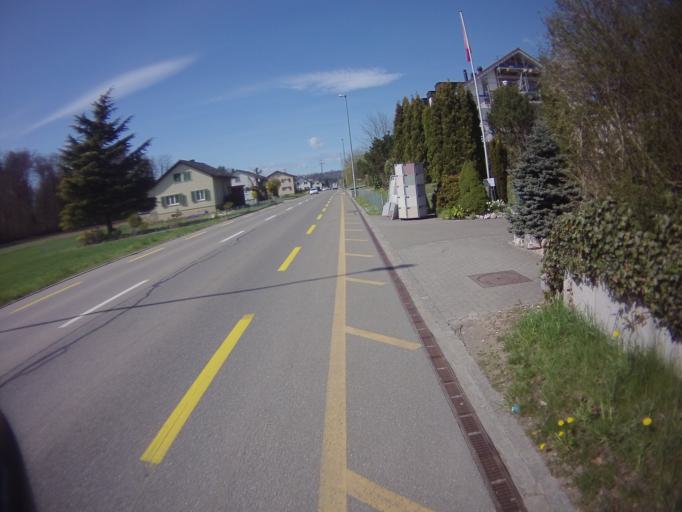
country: CH
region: Aargau
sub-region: Bezirk Baden
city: Niederrohrdorf
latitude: 47.4388
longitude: 8.2977
